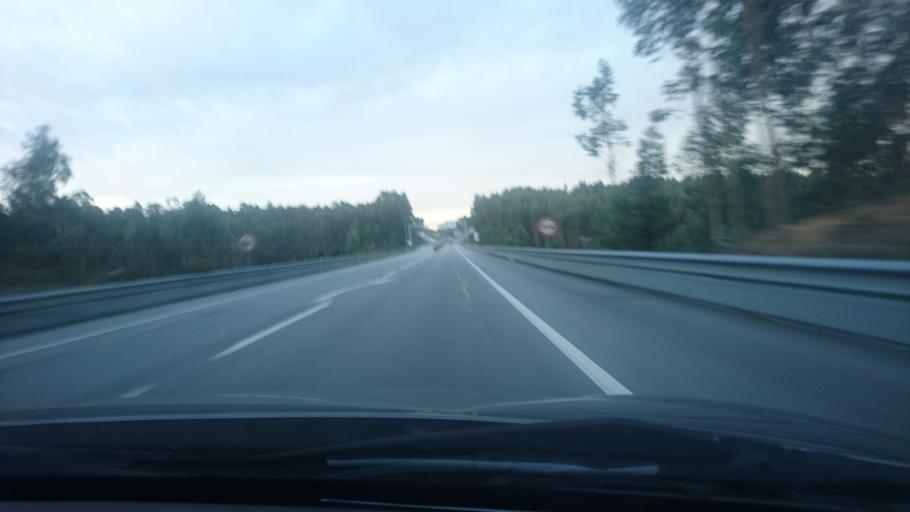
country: PT
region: Aveiro
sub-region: Santa Maria da Feira
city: Milheiros de Poiares
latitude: 40.9288
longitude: -8.4832
